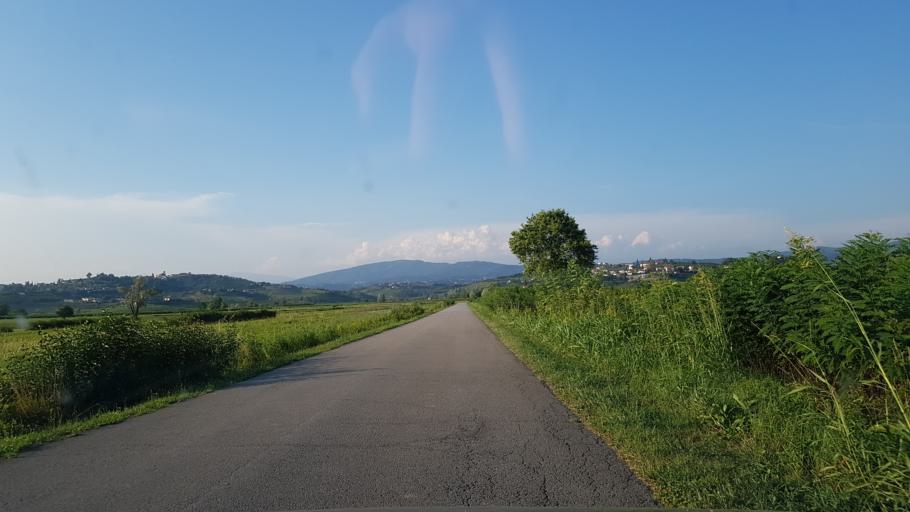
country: IT
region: Friuli Venezia Giulia
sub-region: Provincia di Gorizia
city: Capriva del Friuli
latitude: 45.9609
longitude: 13.5236
